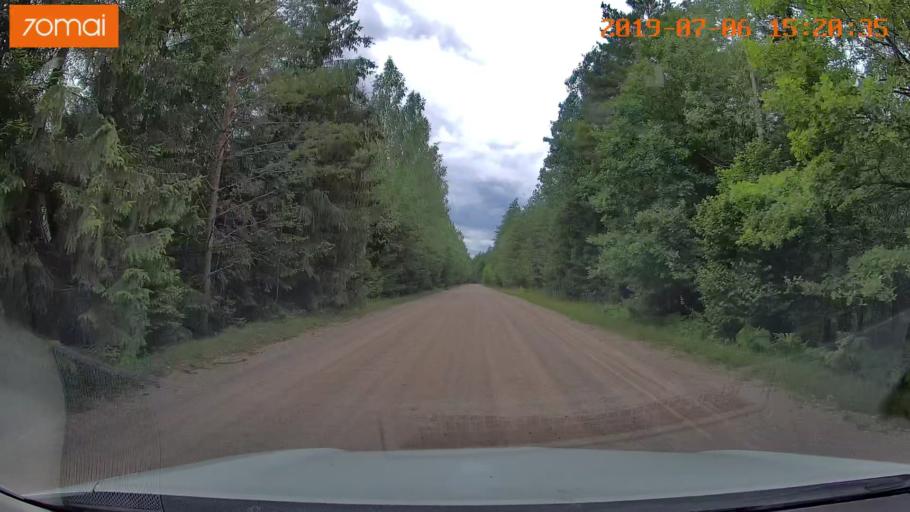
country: BY
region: Minsk
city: Valozhyn
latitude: 54.0070
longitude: 26.6322
